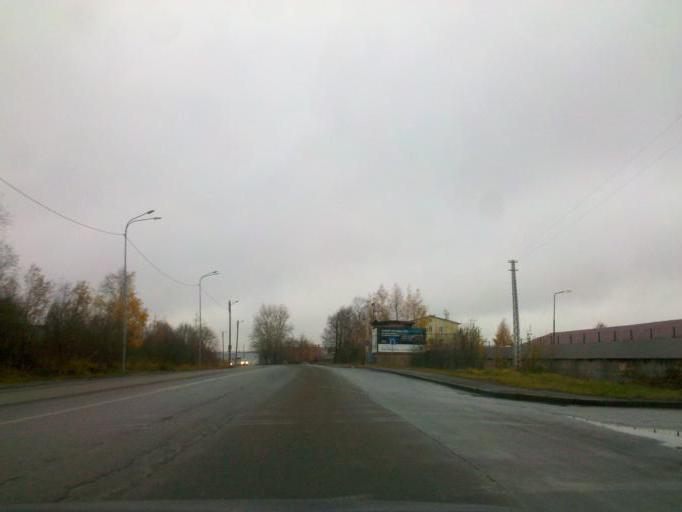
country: RU
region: Republic of Karelia
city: Petrozavodsk
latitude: 61.8146
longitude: 34.2852
